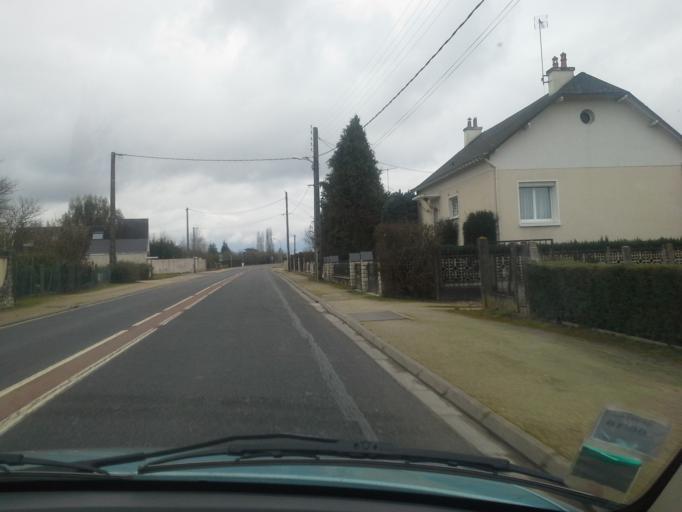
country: FR
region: Centre
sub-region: Departement du Loir-et-Cher
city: Villiers-sur-Loir
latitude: 47.8048
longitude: 0.9937
